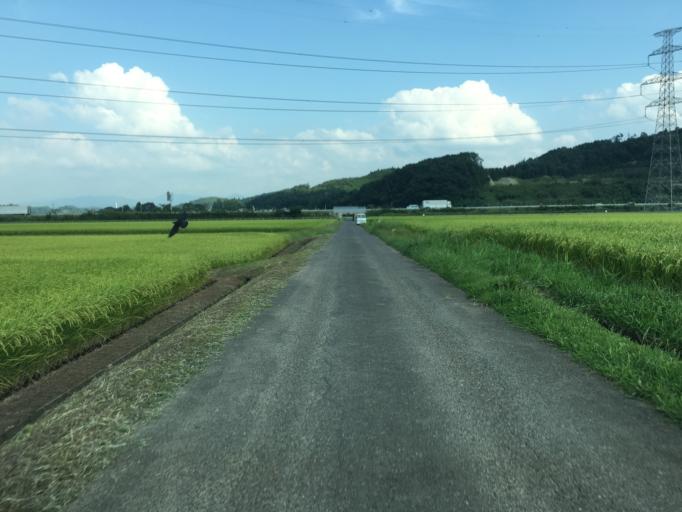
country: JP
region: Fukushima
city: Motomiya
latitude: 37.5541
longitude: 140.3899
